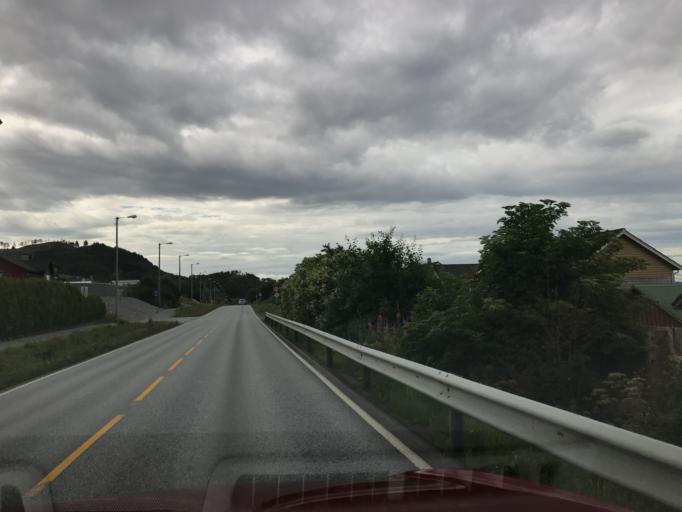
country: NO
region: Rogaland
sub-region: Strand
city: Tau
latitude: 59.0524
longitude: 5.9193
